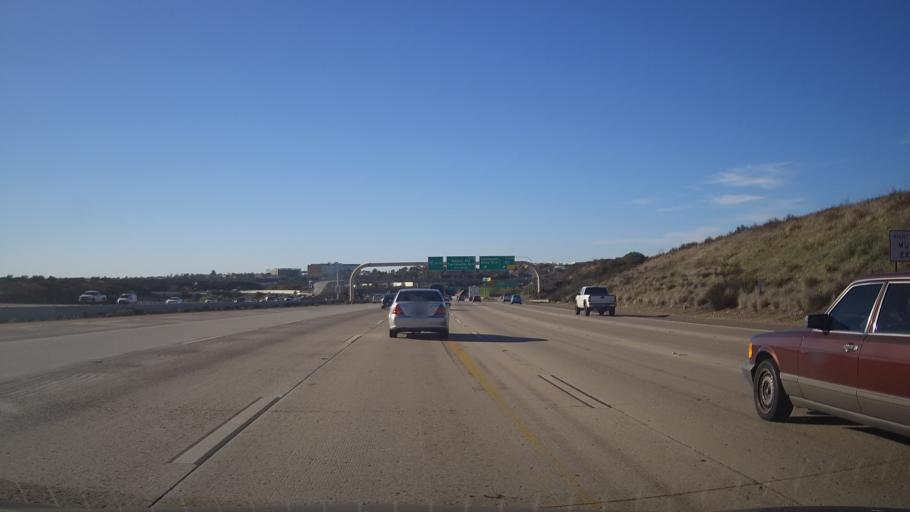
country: US
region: California
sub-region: San Diego County
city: La Mesa
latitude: 32.8479
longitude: -117.1178
